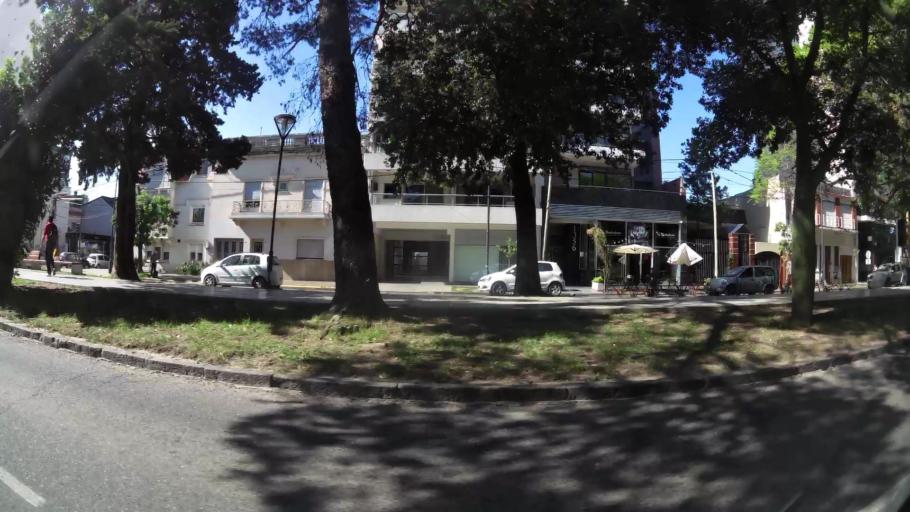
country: AR
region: Santa Fe
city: Santa Fe de la Vera Cruz
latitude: -31.6385
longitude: -60.6897
